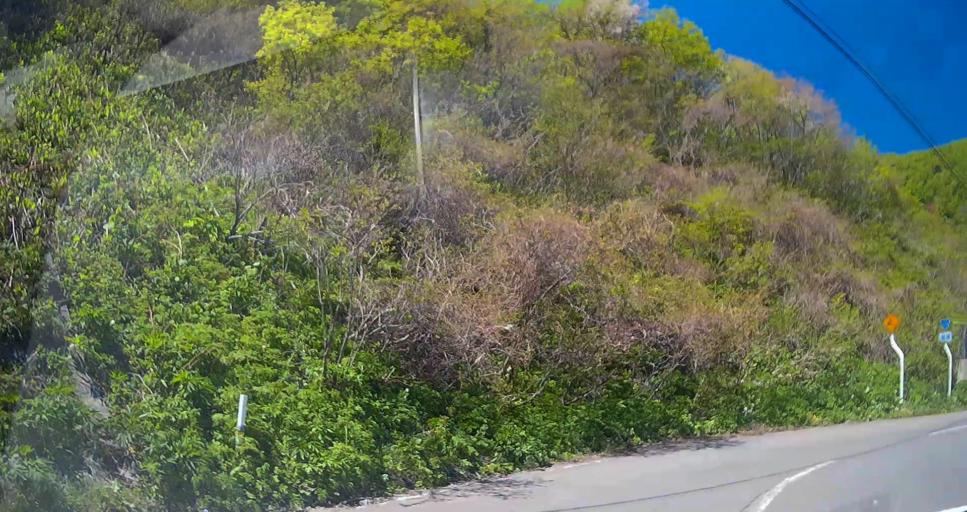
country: JP
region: Aomori
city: Mutsu
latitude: 41.3256
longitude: 140.8138
